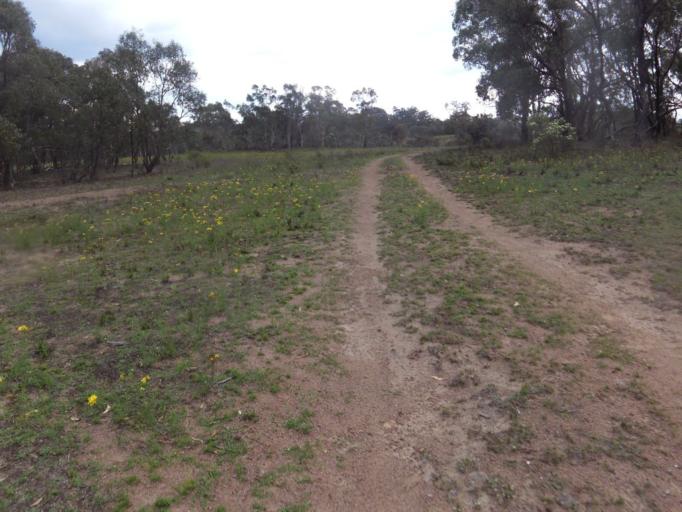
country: AU
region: Australian Capital Territory
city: Forrest
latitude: -35.3504
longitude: 149.1228
